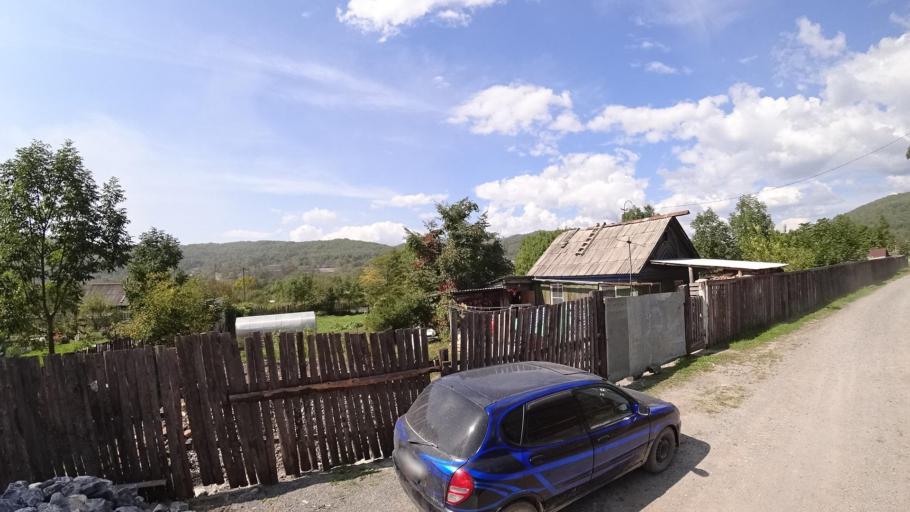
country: RU
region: Jewish Autonomous Oblast
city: Londoko
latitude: 49.0248
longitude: 131.9325
